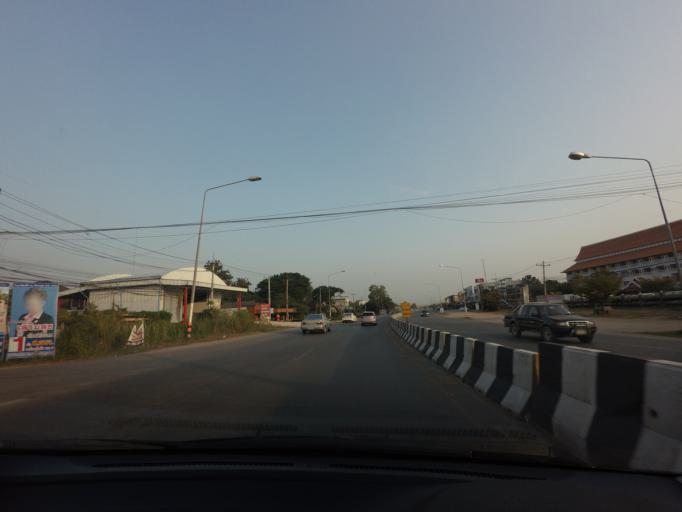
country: TH
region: Sukhothai
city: Sukhothai
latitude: 17.0198
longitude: 99.8279
